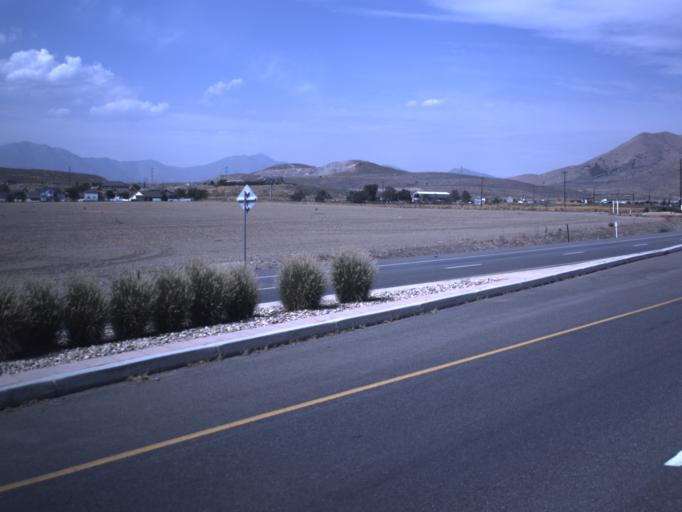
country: US
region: Utah
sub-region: Utah County
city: Saratoga Springs
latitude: 40.3827
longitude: -111.9288
